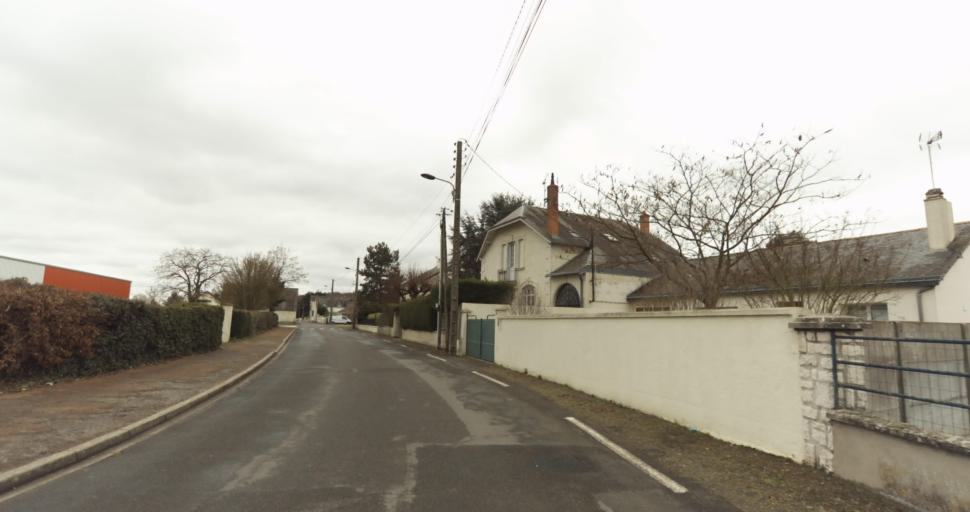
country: FR
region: Pays de la Loire
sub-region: Departement de Maine-et-Loire
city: Distre
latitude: 47.2398
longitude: -0.0939
